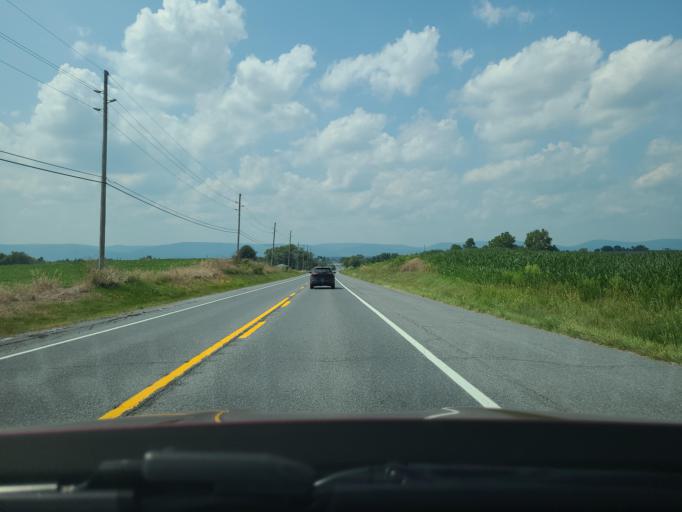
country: US
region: Maryland
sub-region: Frederick County
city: Woodsboro
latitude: 39.5491
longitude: -77.3312
